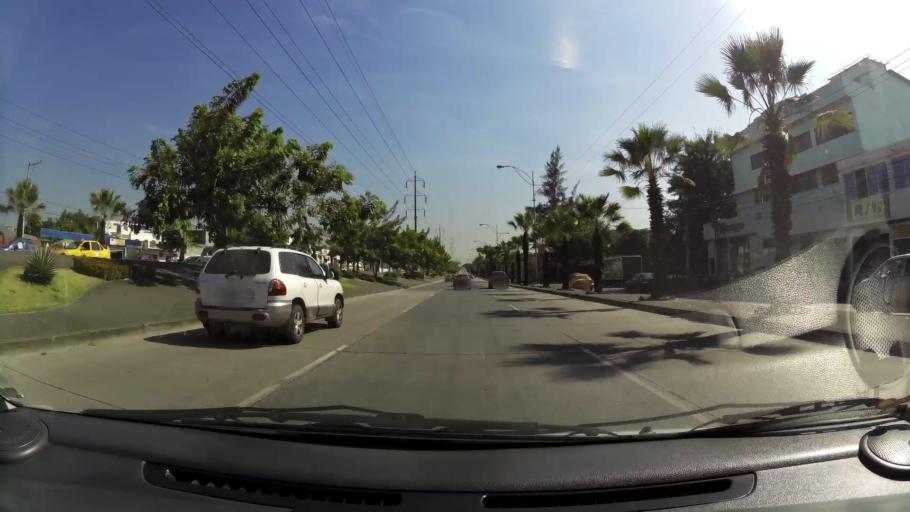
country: EC
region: Guayas
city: Eloy Alfaro
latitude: -2.1194
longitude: -79.9057
